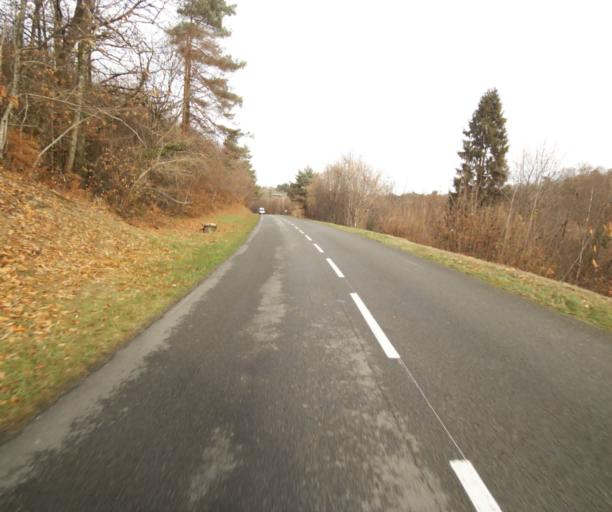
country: FR
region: Limousin
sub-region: Departement de la Correze
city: Chameyrat
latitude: 45.2587
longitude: 1.7051
